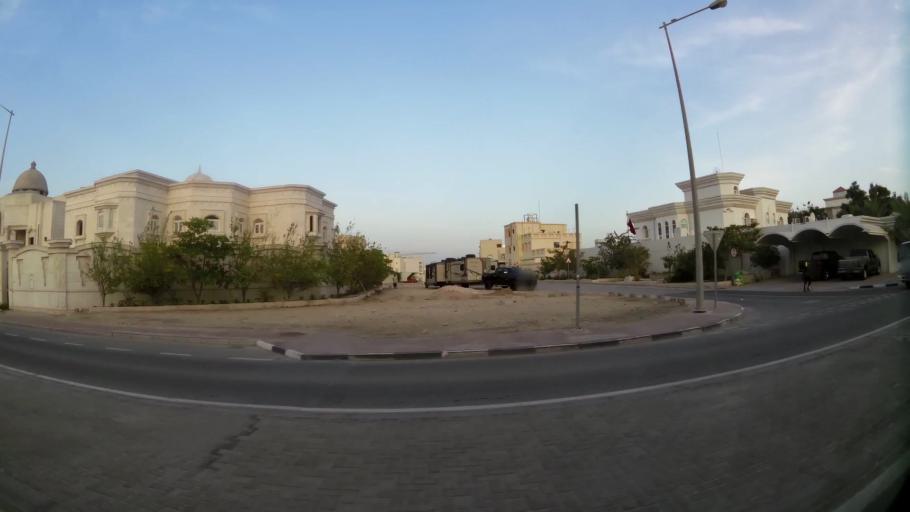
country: QA
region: Al Wakrah
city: Al Wakrah
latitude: 25.1894
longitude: 51.6063
